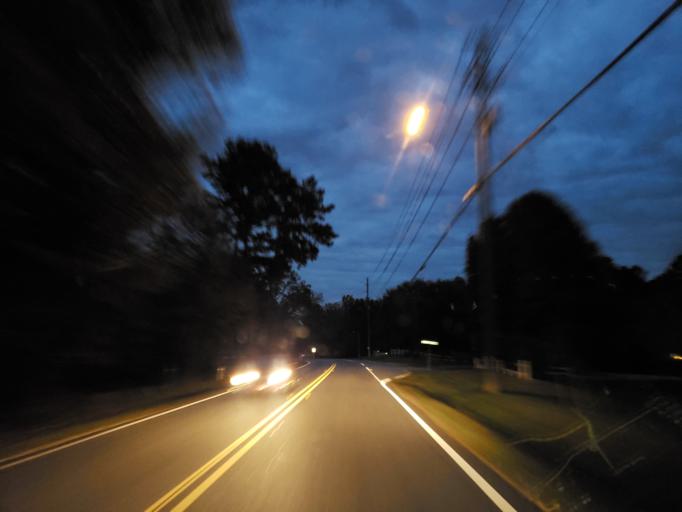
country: US
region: Georgia
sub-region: Cobb County
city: Powder Springs
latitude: 33.8880
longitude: -84.7062
